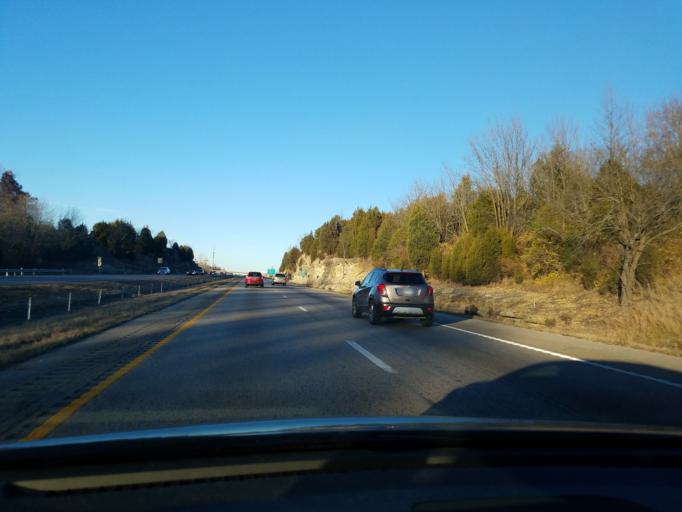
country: US
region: Missouri
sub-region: Franklin County
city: Villa Ridge
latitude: 38.4666
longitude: -90.8544
